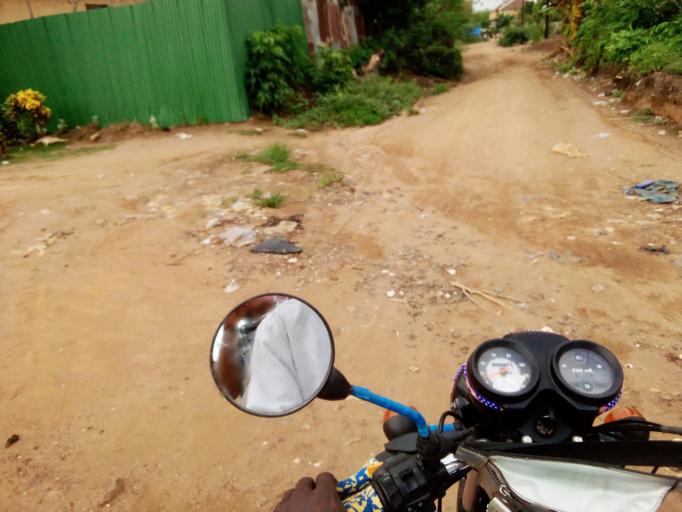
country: SL
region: Western Area
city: Waterloo
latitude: 8.3420
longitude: -13.0699
